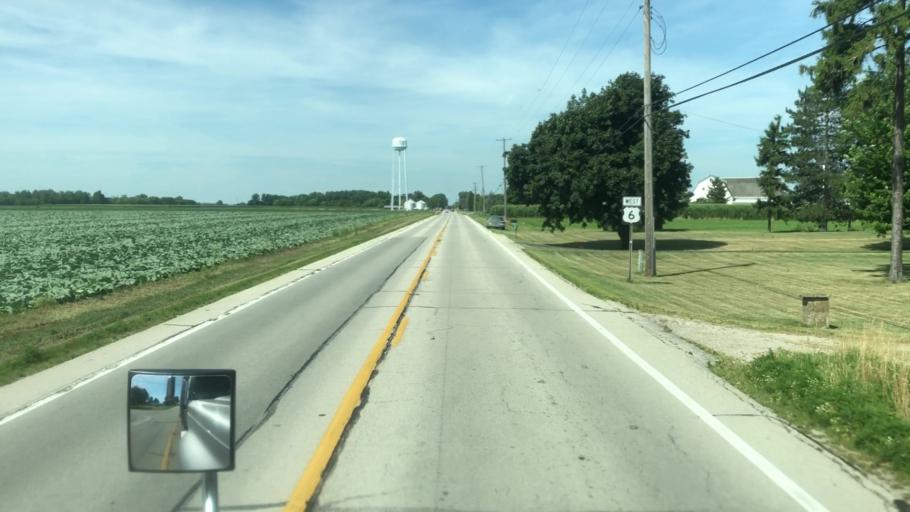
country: US
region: Ohio
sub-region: Ottawa County
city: Port Clinton
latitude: 41.4160
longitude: -82.8946
